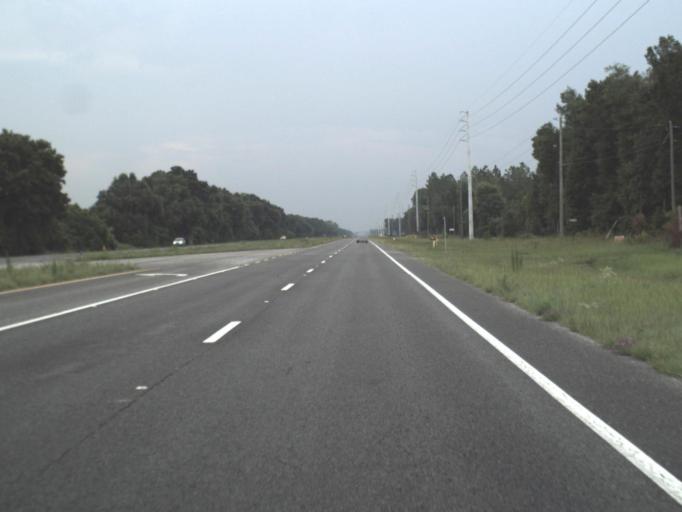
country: US
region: Florida
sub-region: Levy County
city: Chiefland
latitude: 29.4748
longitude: -82.7984
